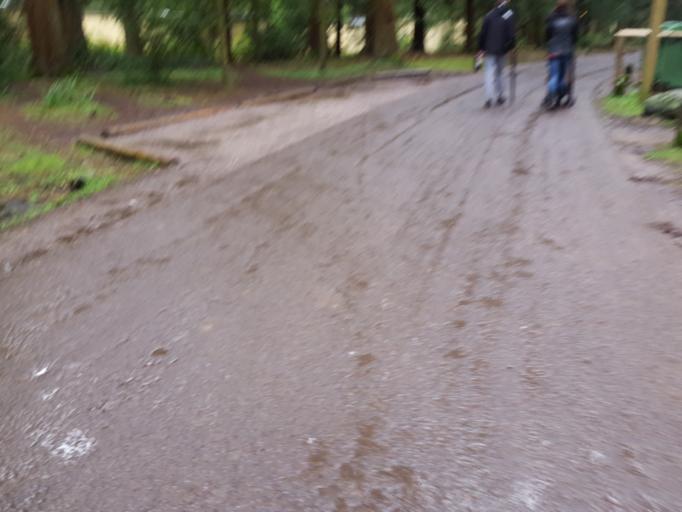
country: GB
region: England
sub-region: Wiltshire
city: Corsley
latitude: 51.1792
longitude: -2.2409
